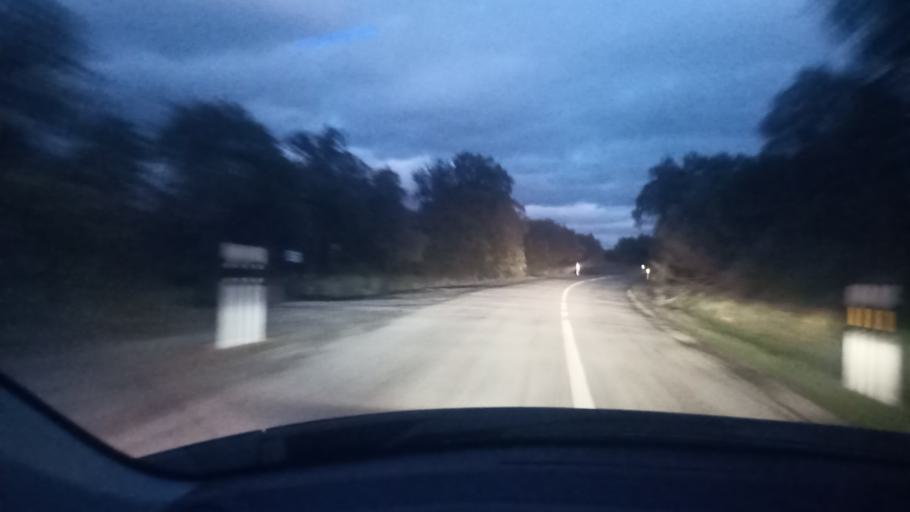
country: ES
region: Madrid
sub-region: Provincia de Madrid
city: Colmenar del Arroyo
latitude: 40.4307
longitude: -4.2229
